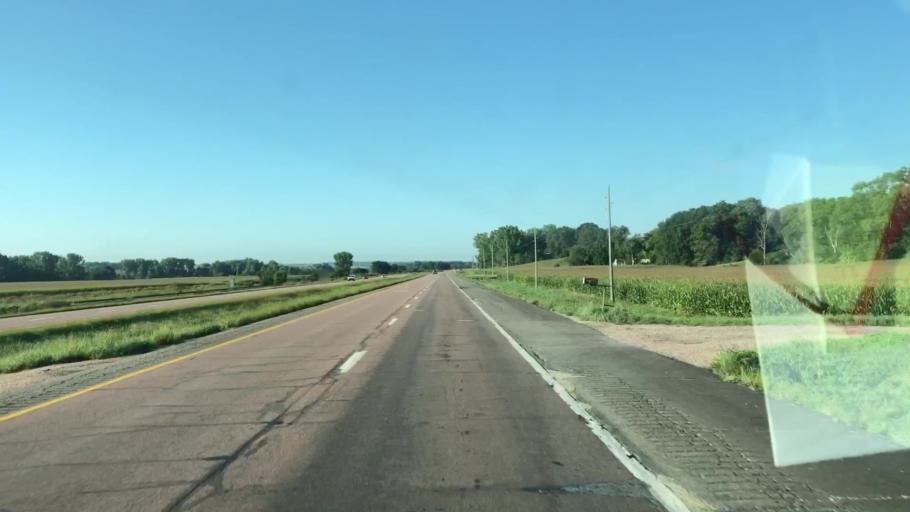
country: US
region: Iowa
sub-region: Woodbury County
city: Sioux City
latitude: 42.5906
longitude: -96.3069
